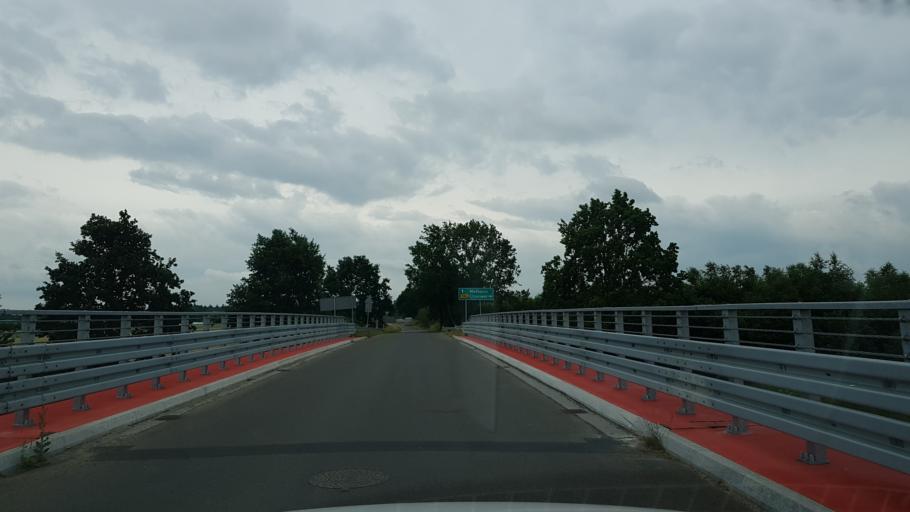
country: PL
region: West Pomeranian Voivodeship
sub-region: Powiat goleniowski
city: Maszewo
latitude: 53.4296
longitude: 14.9970
